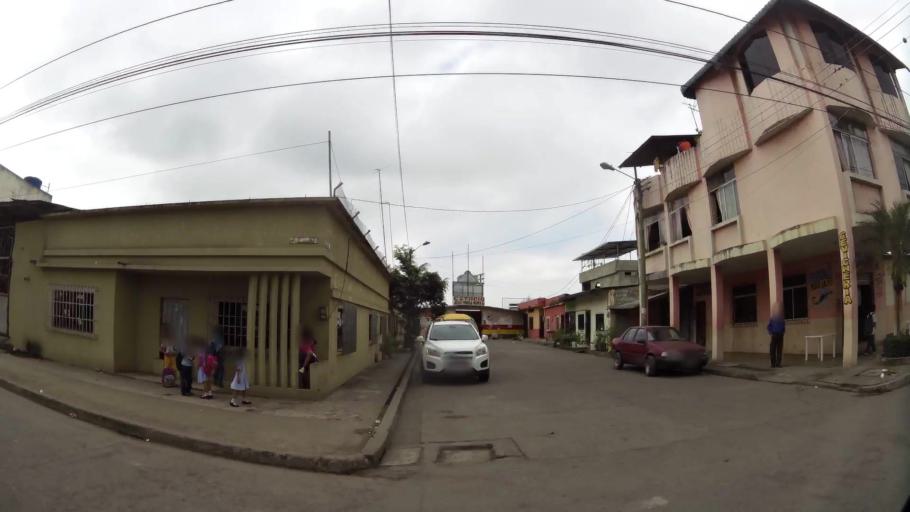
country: EC
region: El Oro
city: Pasaje
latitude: -3.2449
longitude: -79.8332
